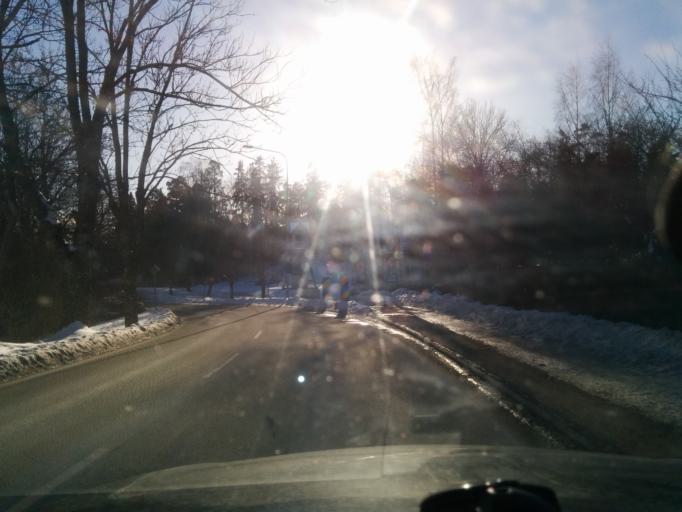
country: SE
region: Stockholm
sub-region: Taby Kommun
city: Taby
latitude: 59.4634
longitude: 18.0873
